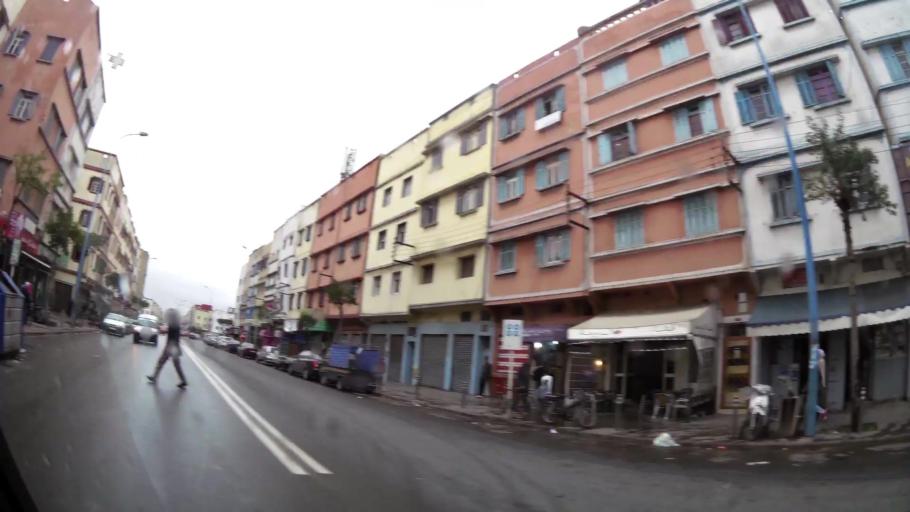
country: MA
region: Grand Casablanca
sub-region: Casablanca
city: Casablanca
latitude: 33.5554
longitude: -7.5739
